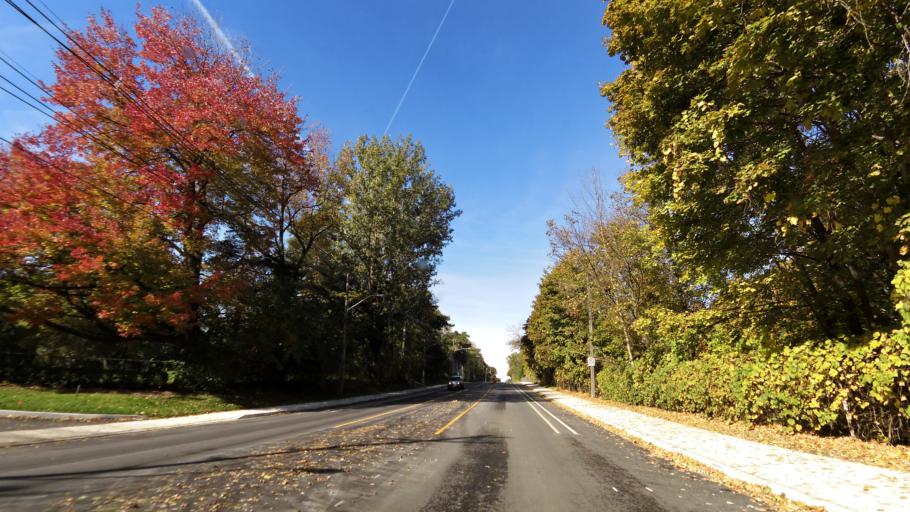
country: CA
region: Ontario
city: Etobicoke
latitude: 43.5879
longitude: -79.5559
